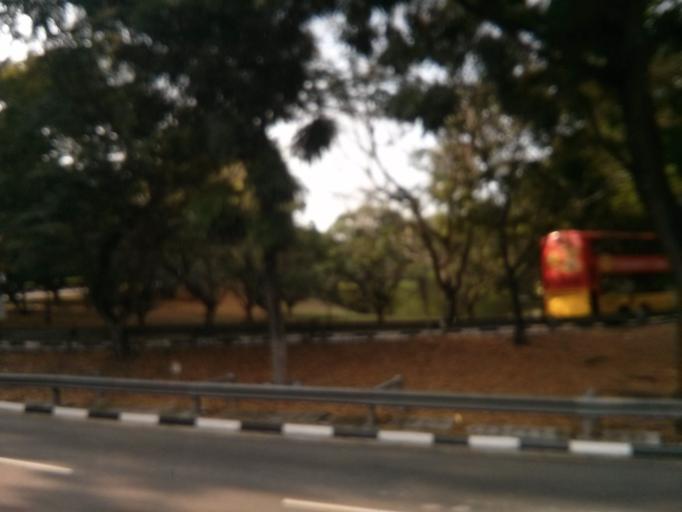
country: SG
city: Singapore
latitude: 1.2929
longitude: 103.7864
